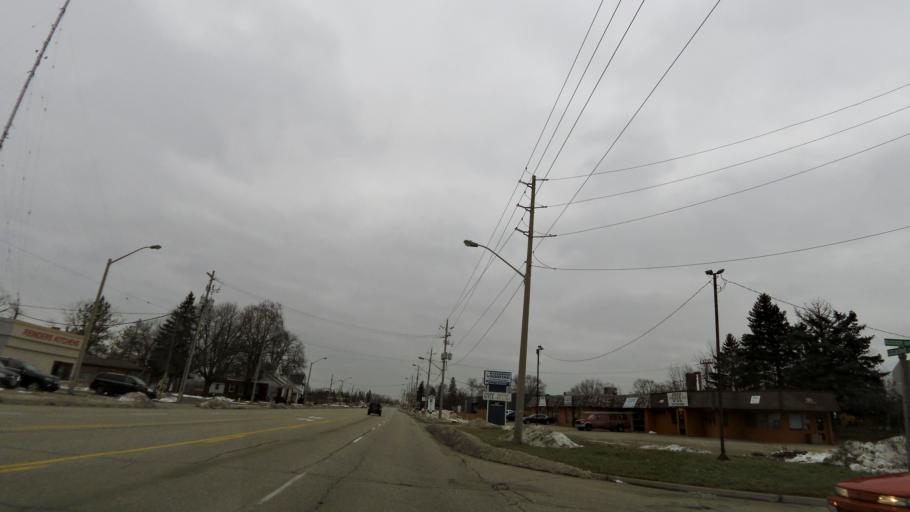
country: CA
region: Ontario
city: Brantford
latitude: 43.1459
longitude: -80.1991
